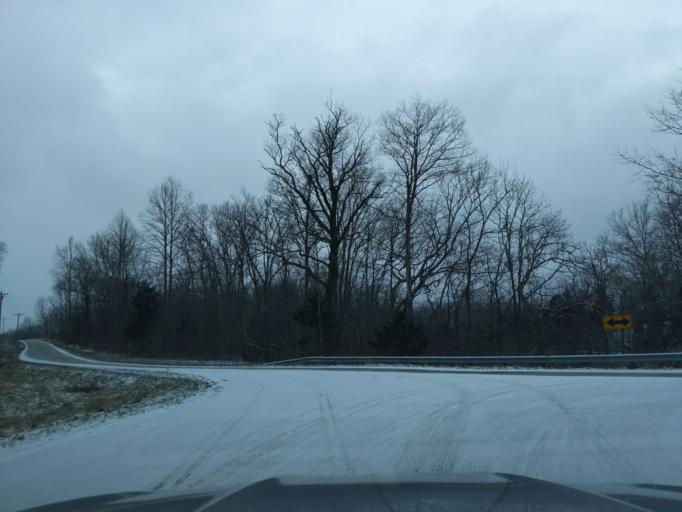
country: US
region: Indiana
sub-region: Decatur County
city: Greensburg
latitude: 39.2461
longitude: -85.4685
